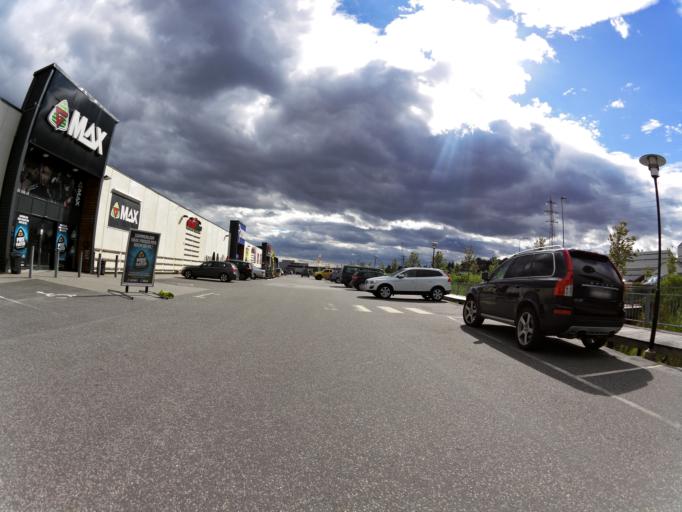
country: NO
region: Ostfold
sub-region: Fredrikstad
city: Fredrikstad
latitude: 59.2511
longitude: 10.9951
